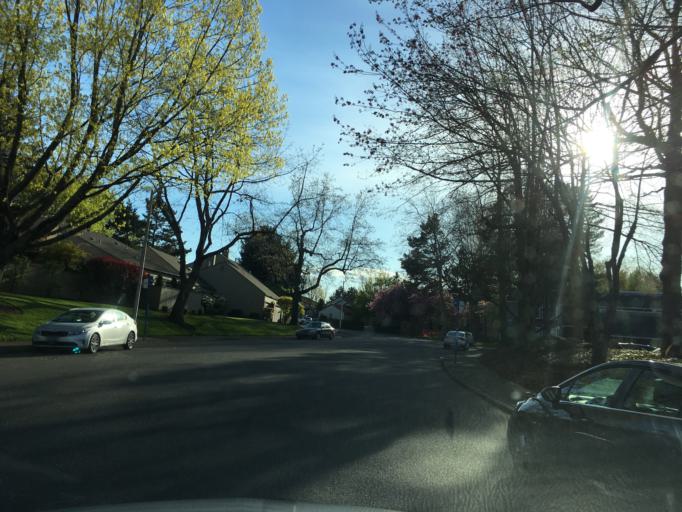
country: US
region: Oregon
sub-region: Multnomah County
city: Lents
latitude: 45.5533
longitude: -122.5331
